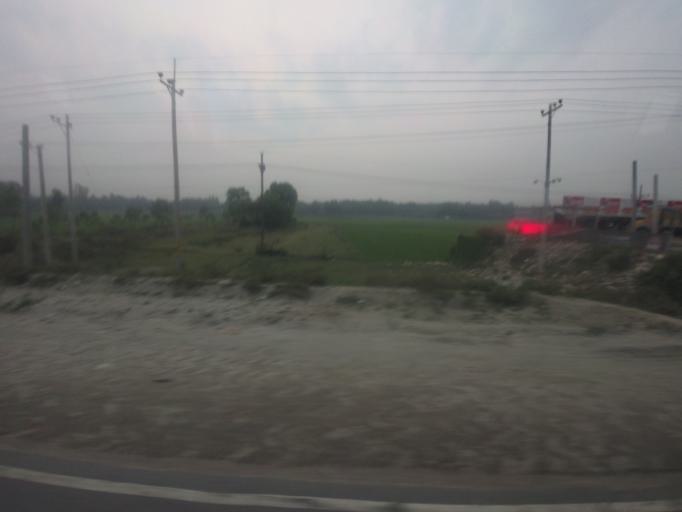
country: BD
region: Dhaka
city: Tangail
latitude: 24.3074
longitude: 89.9206
